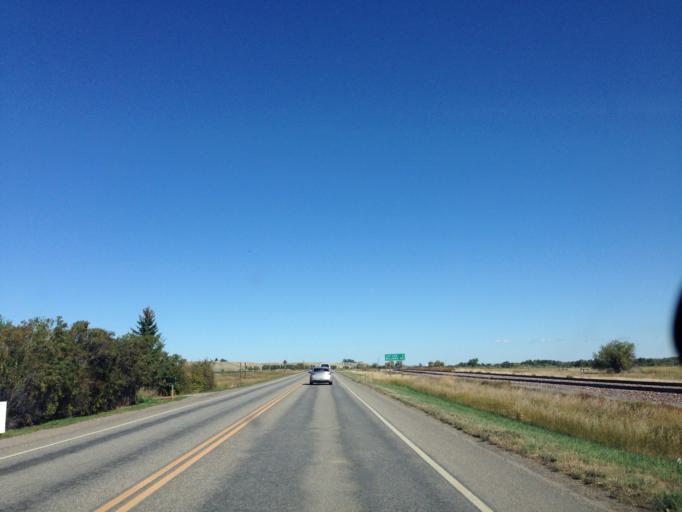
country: US
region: Montana
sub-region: Yellowstone County
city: Laurel
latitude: 45.5579
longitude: -108.8410
